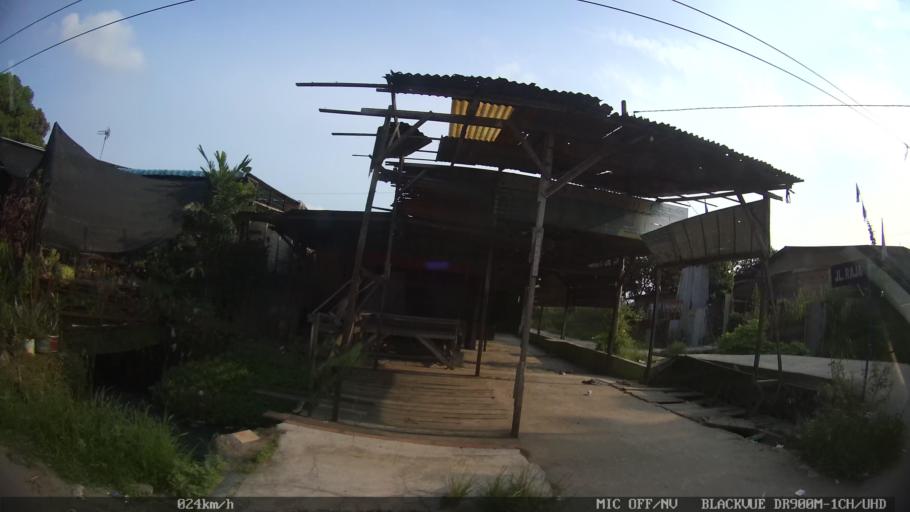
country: ID
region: North Sumatra
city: Medan
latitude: 3.5813
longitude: 98.7481
